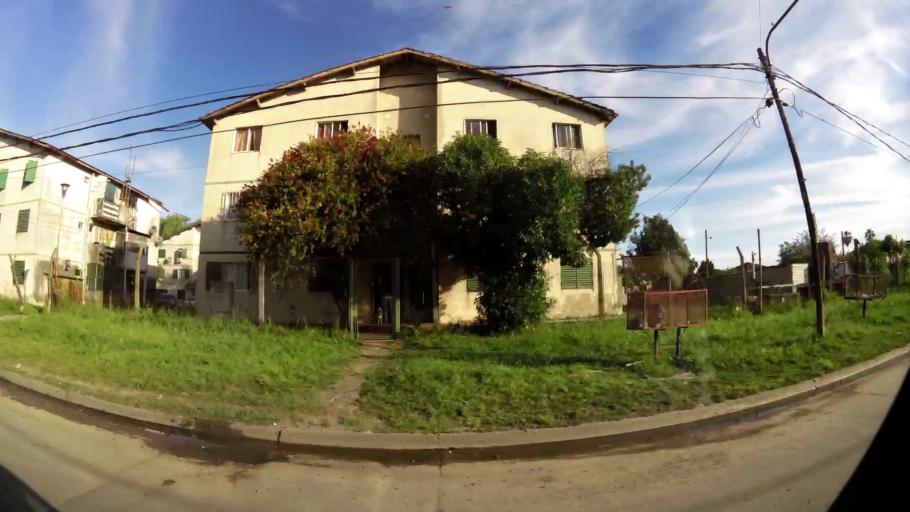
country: AR
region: Buenos Aires
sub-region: Partido de Almirante Brown
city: Adrogue
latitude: -34.8162
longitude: -58.3317
